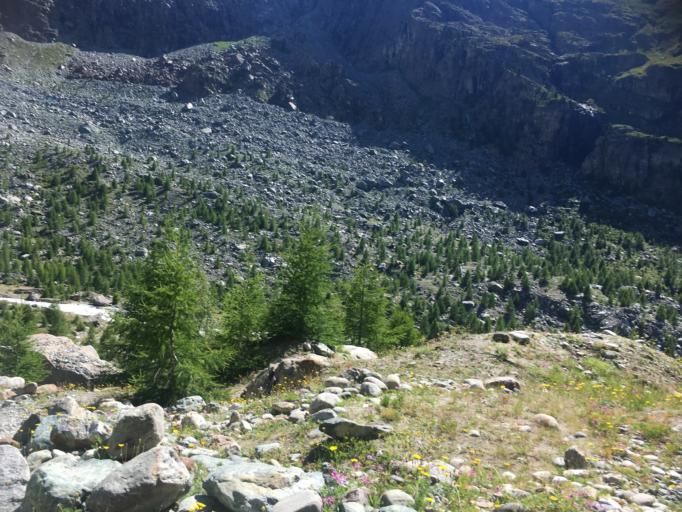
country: CH
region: Valais
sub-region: Visp District
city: Zermatt
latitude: 45.9898
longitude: 7.7350
